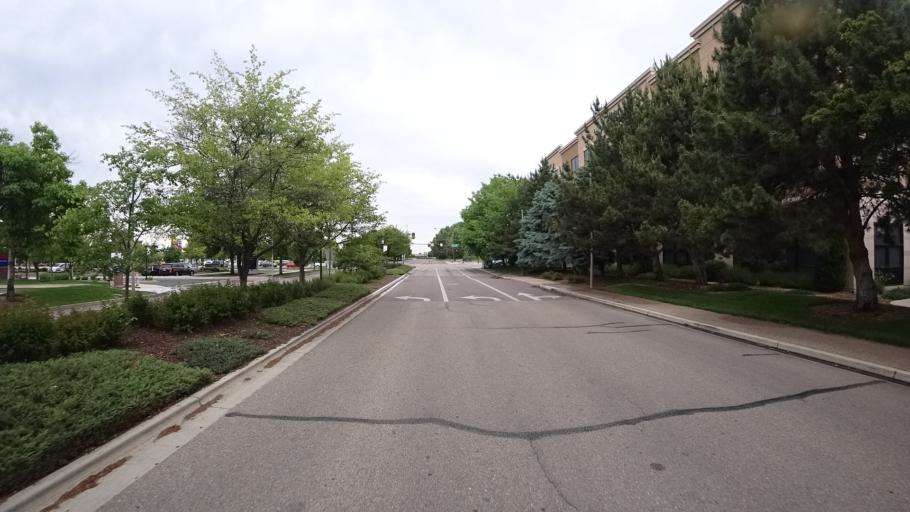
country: US
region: Idaho
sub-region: Ada County
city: Meridian
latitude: 43.6012
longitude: -116.3536
